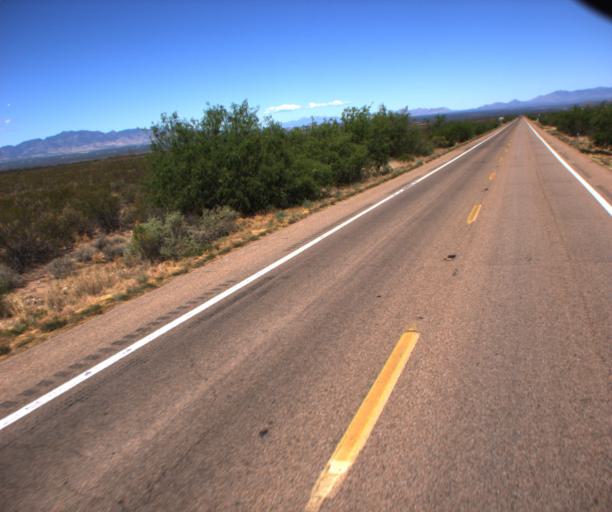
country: US
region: Arizona
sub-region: Cochise County
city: Bisbee
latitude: 31.5282
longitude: -110.0517
